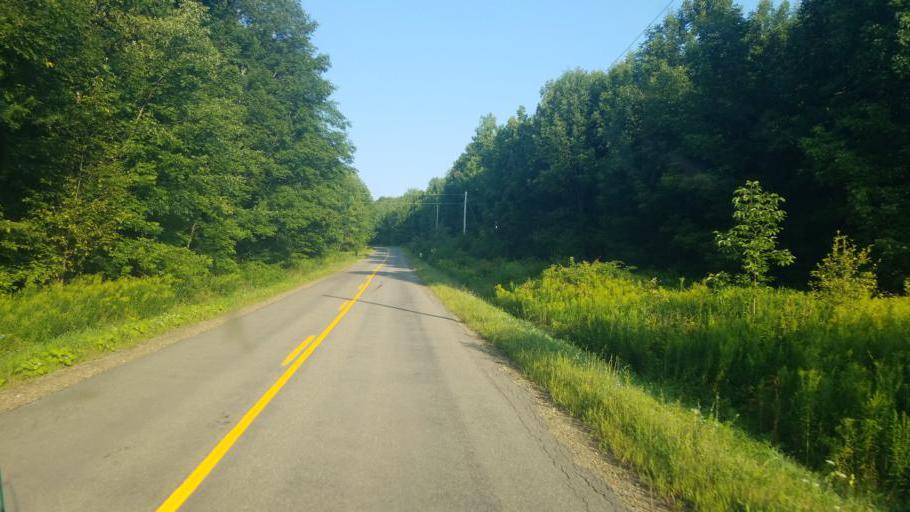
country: US
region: Pennsylvania
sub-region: Tioga County
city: Westfield
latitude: 42.0655
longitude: -77.6280
